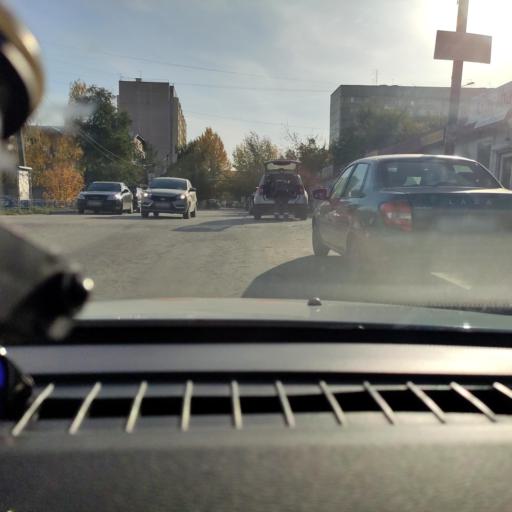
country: RU
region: Samara
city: Samara
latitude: 53.1074
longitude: 50.0805
